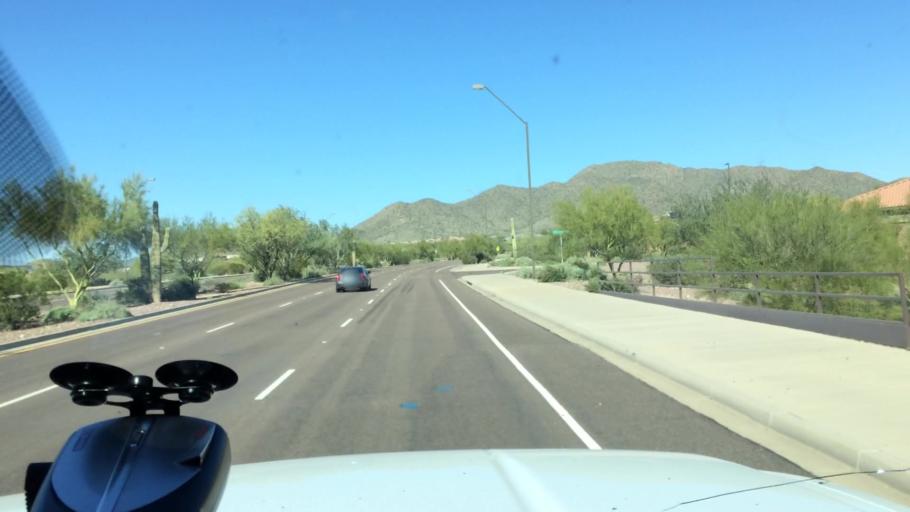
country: US
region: Arizona
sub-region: Maricopa County
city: Anthem
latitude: 33.8529
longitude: -112.1155
